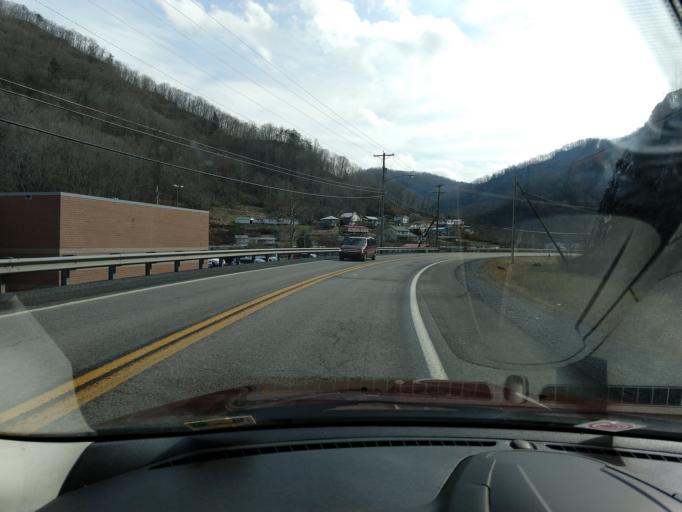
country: US
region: West Virginia
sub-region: McDowell County
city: Welch
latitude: 37.3570
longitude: -81.8018
